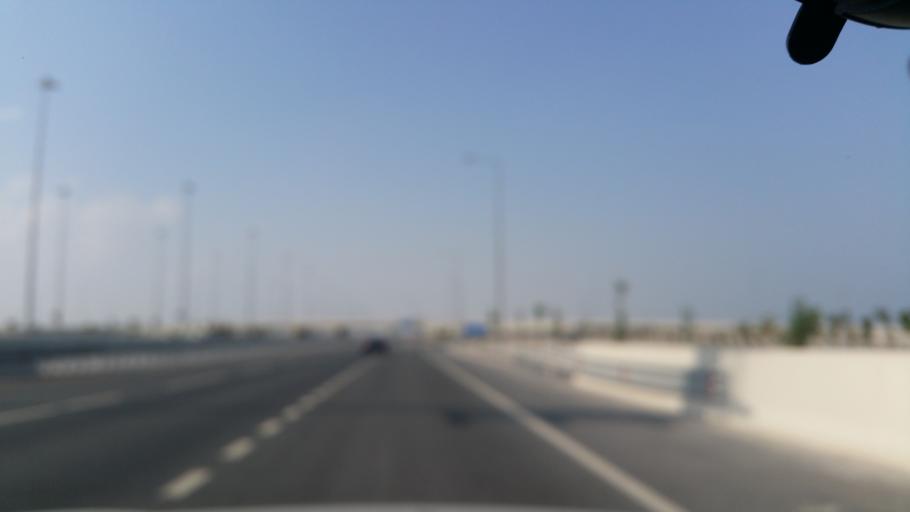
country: QA
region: Baladiyat Umm Salal
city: Umm Salal Muhammad
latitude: 25.4523
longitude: 51.4797
